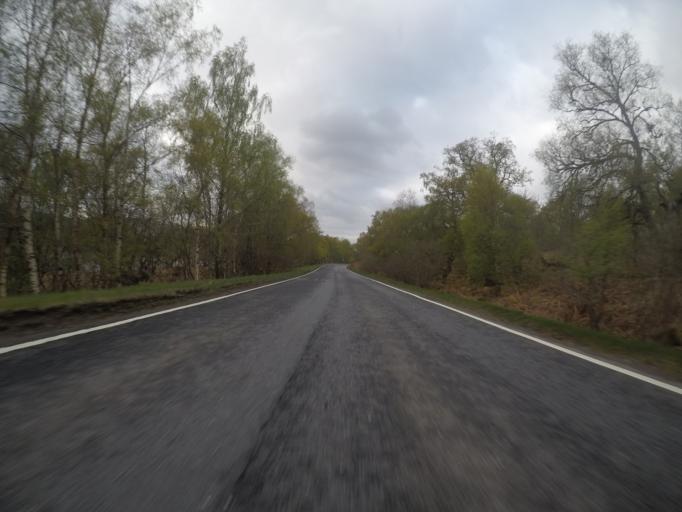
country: GB
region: Scotland
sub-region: Highland
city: Kingussie
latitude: 56.9676
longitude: -4.4404
